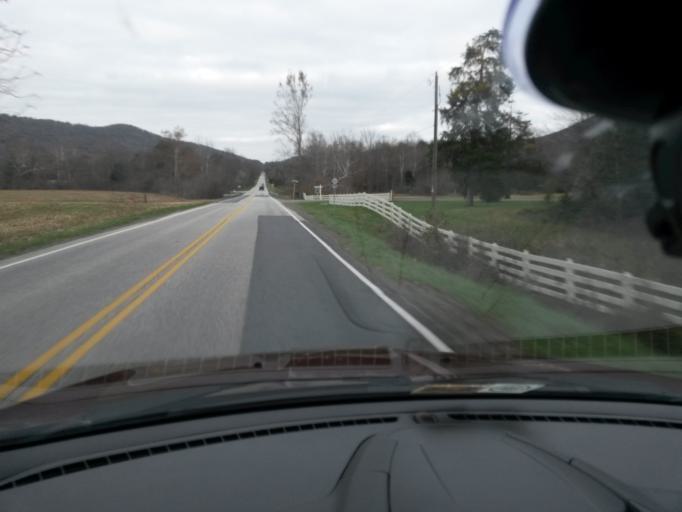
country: US
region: Virginia
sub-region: Rockbridge County
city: Glasgow
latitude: 37.6484
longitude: -79.4291
